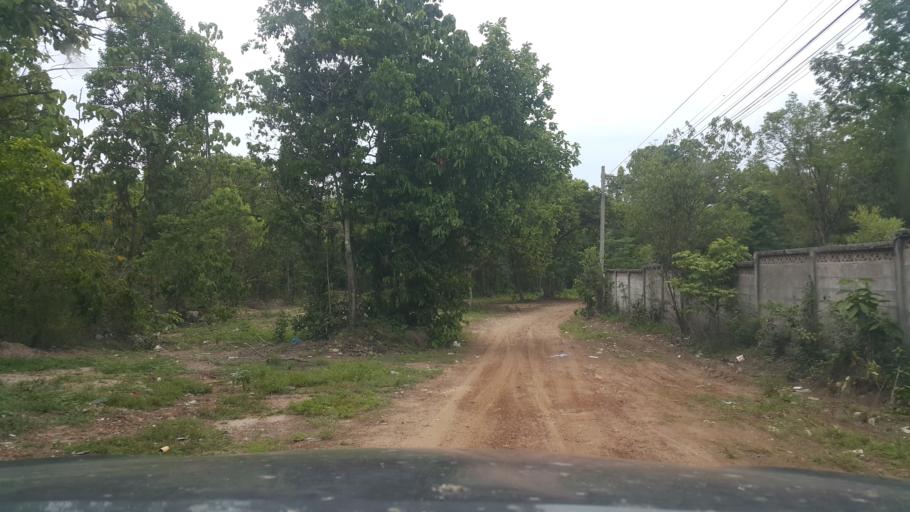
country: TH
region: Chiang Mai
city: San Pa Tong
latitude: 18.6487
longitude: 98.8464
